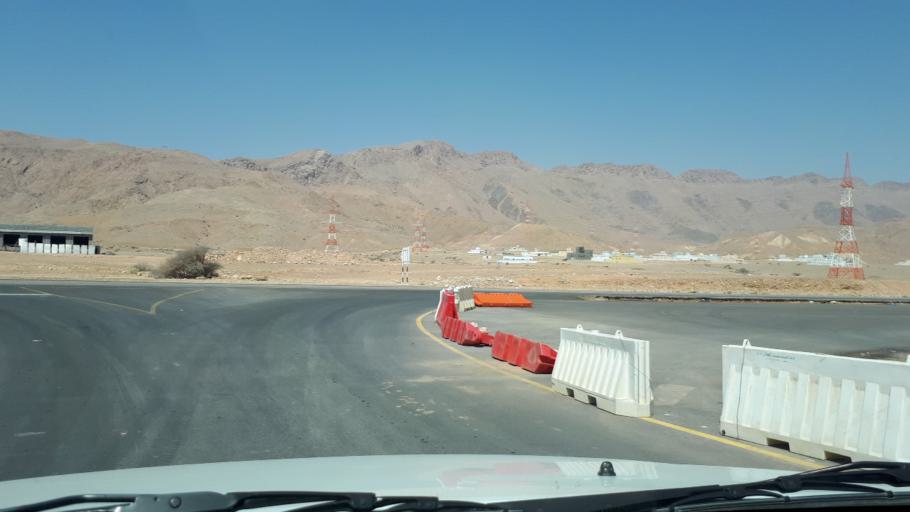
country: OM
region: Ash Sharqiyah
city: Sur
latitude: 22.6031
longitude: 59.4316
